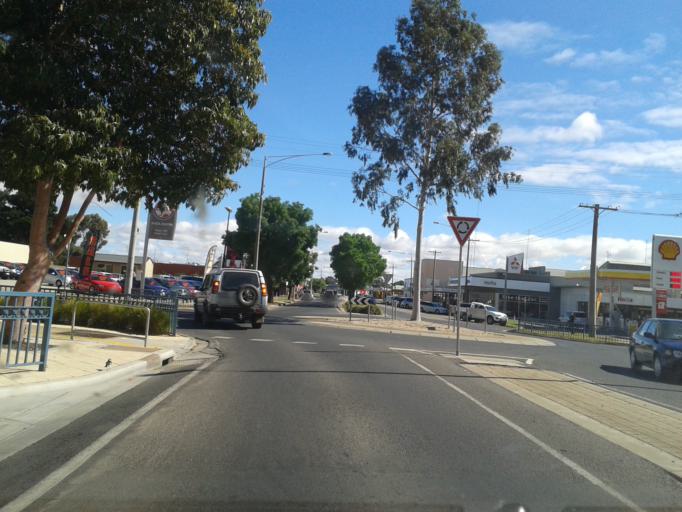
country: AU
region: Victoria
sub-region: Swan Hill
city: Swan Hill
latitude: -35.3367
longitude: 143.5588
